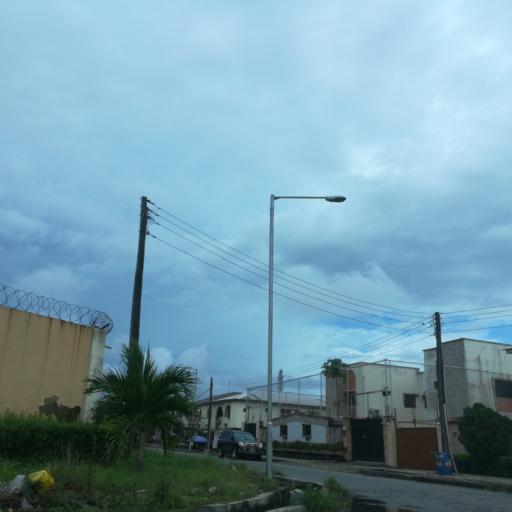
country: NG
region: Lagos
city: Ikoyi
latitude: 6.4387
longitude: 3.4779
